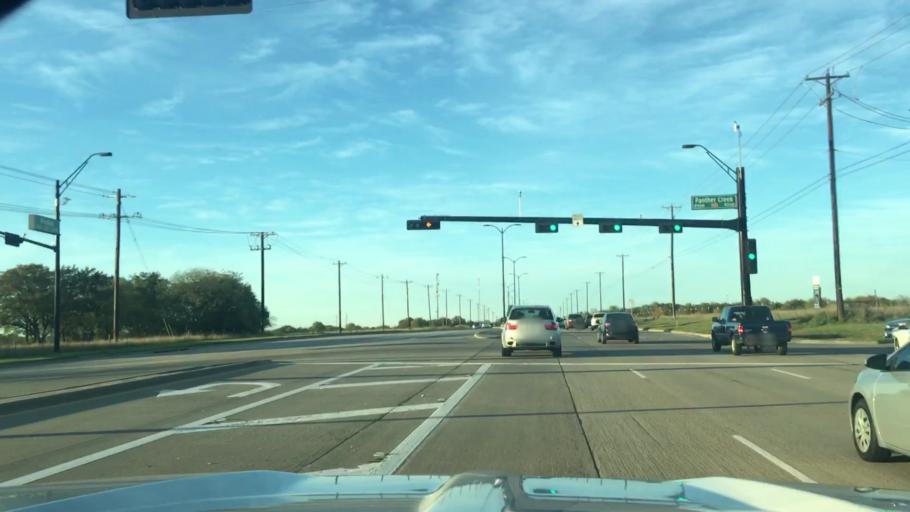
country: US
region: Texas
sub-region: Collin County
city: Frisco
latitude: 33.1894
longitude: -96.8028
